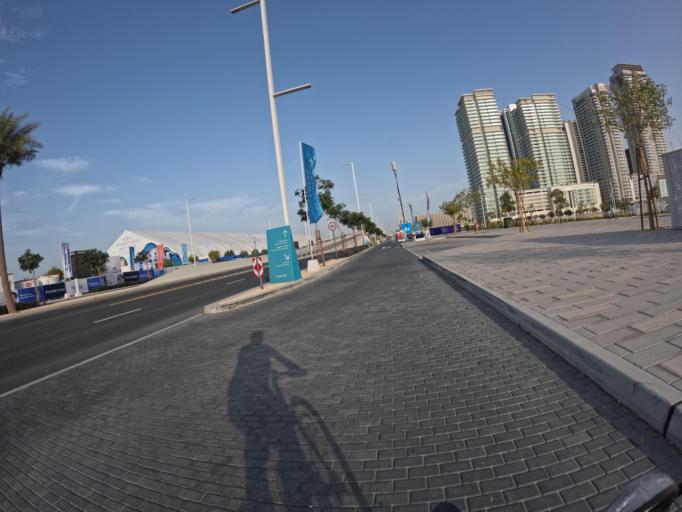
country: AE
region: Dubai
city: Dubai
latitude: 25.0945
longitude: 55.1411
